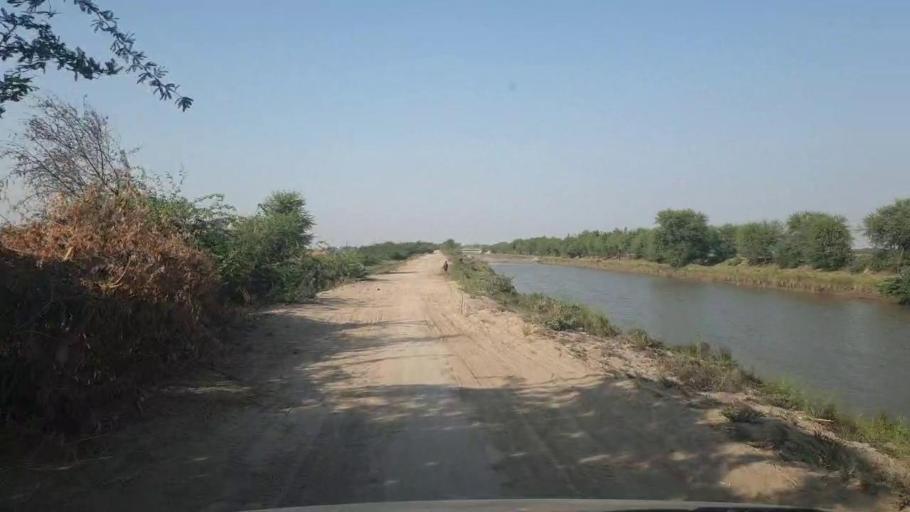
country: PK
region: Sindh
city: Badin
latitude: 24.6349
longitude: 68.8150
